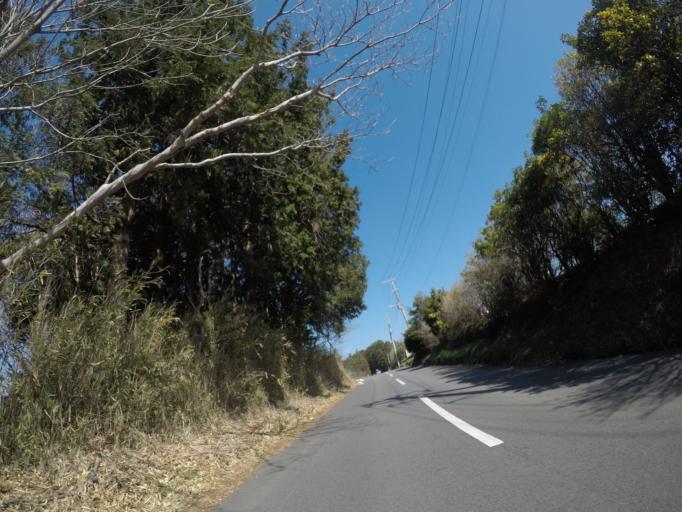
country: JP
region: Shizuoka
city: Numazu
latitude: 35.1420
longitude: 138.8216
